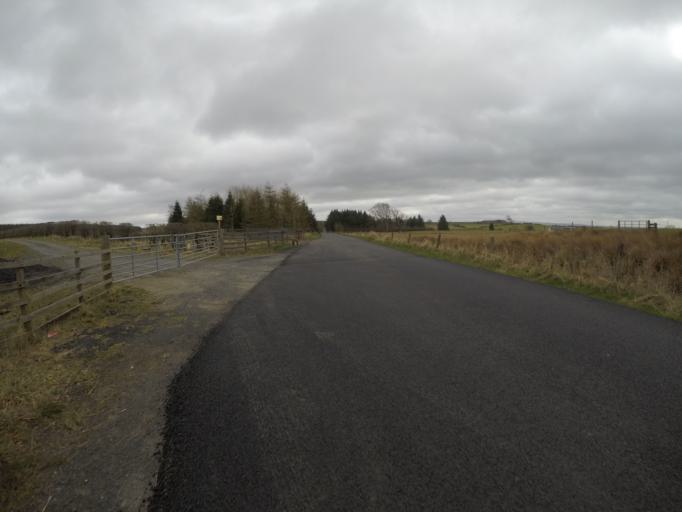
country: GB
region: Scotland
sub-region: East Ayrshire
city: Stewarton
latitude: 55.6809
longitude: -4.4561
